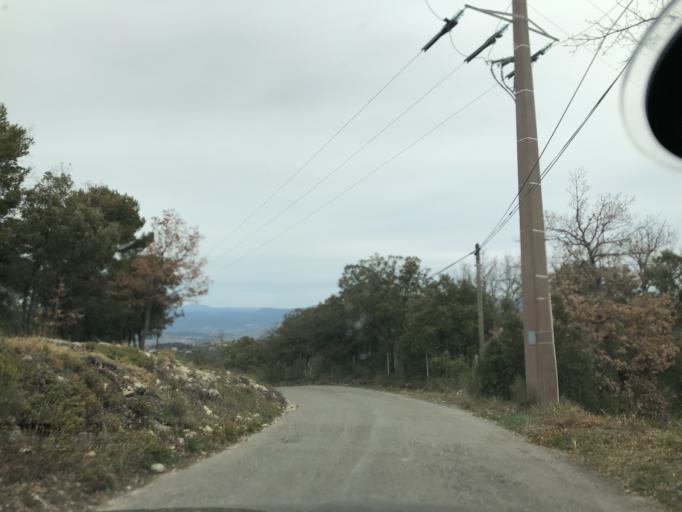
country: FR
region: Provence-Alpes-Cote d'Azur
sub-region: Departement du Vaucluse
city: Bonnieux
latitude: 43.8055
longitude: 5.3131
